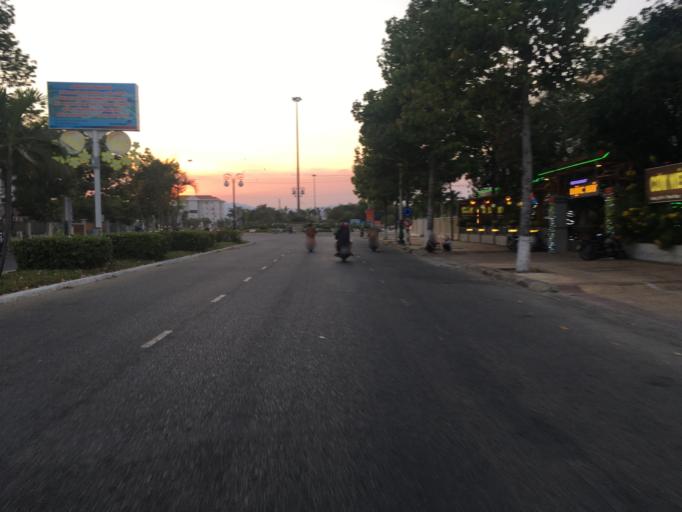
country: VN
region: Ninh Thuan
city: Phan Rang-Thap Cham
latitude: 11.5651
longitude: 109.0021
